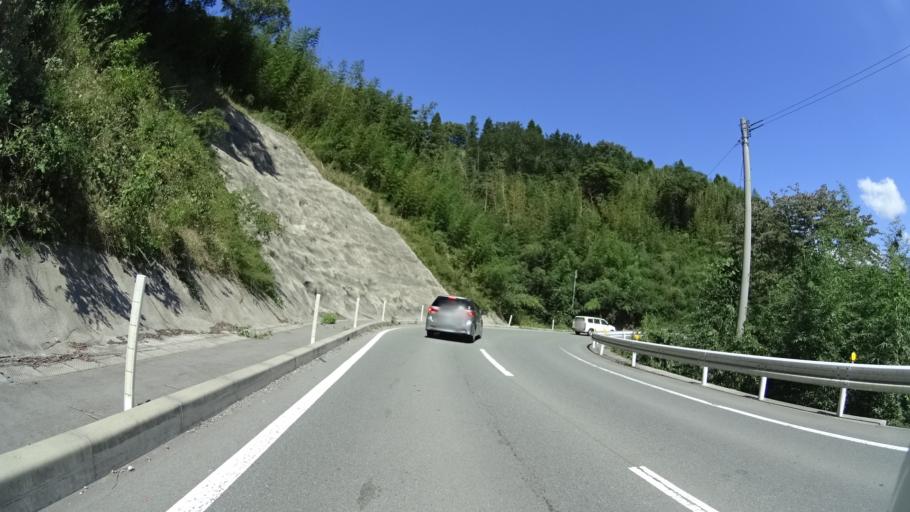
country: JP
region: Kumamoto
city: Aso
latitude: 32.8887
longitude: 130.9938
